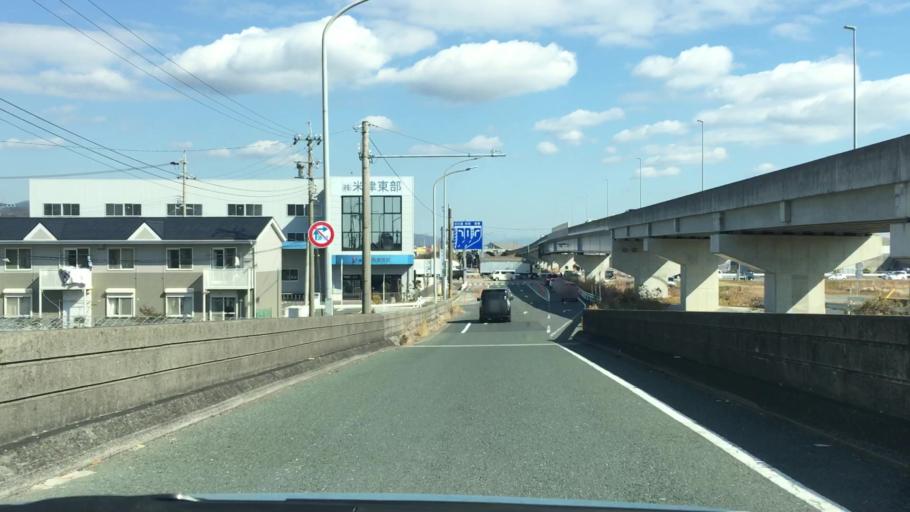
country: JP
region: Aichi
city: Kozakai-cho
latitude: 34.8256
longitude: 137.3383
